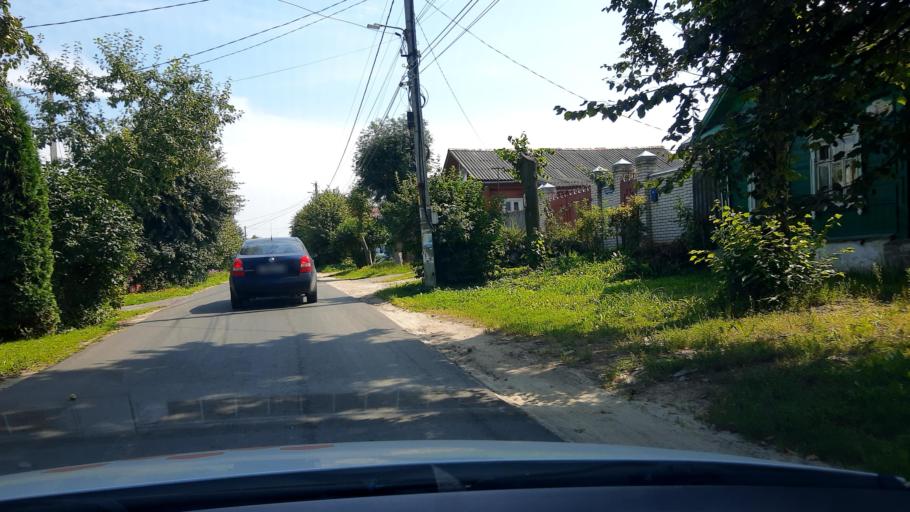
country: RU
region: Moskovskaya
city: Bronnitsy
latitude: 55.4262
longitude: 38.2553
